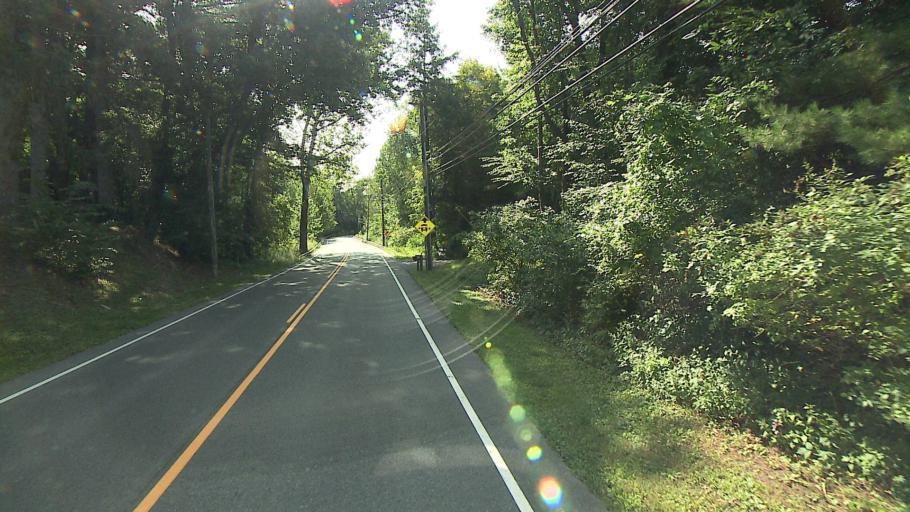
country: US
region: Connecticut
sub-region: Fairfield County
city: Sherman
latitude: 41.6377
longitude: -73.4787
